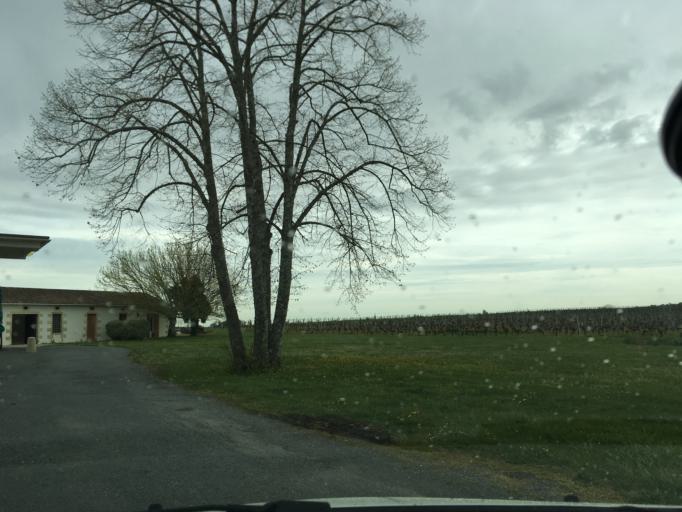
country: FR
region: Aquitaine
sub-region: Departement de la Gironde
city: Lesparre-Medoc
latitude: 45.3134
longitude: -0.8925
